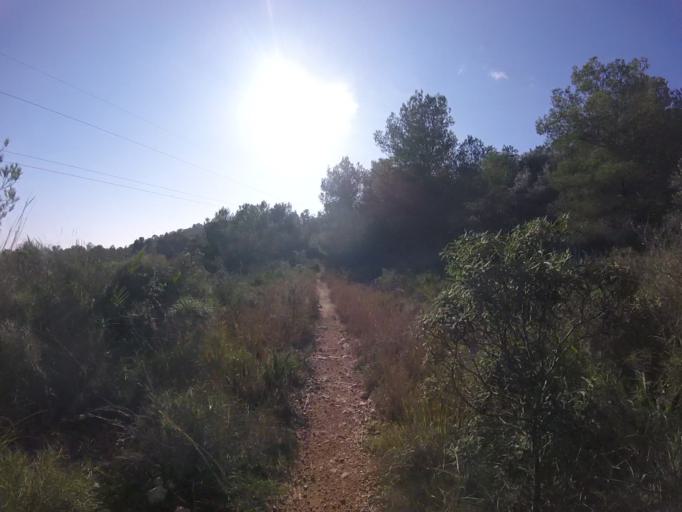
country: ES
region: Valencia
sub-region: Provincia de Castello
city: Santa Magdalena de Pulpis
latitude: 40.3026
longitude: 0.3332
